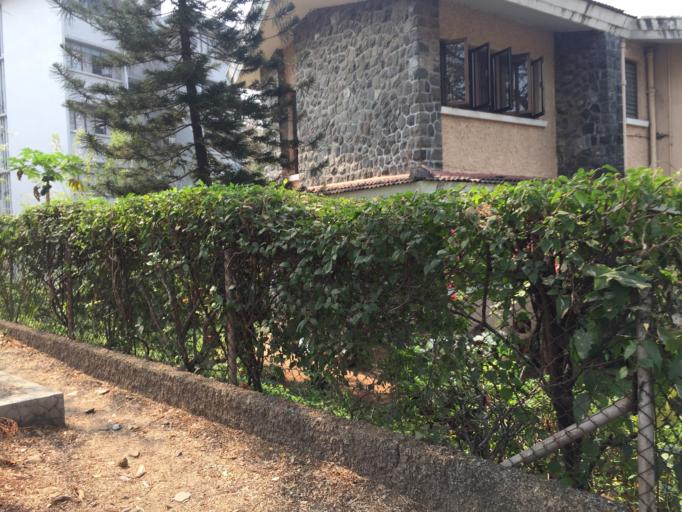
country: IN
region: Maharashtra
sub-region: Mumbai Suburban
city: Powai
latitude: 19.1074
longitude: 72.9220
